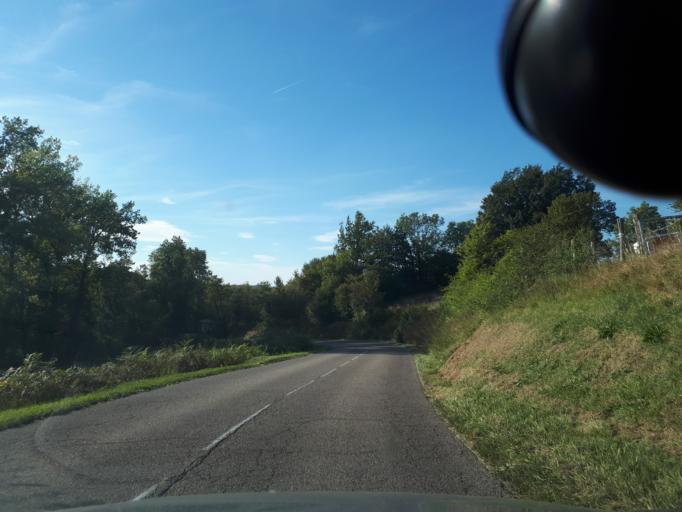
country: FR
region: Rhone-Alpes
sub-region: Departement de l'Isere
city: Maubec
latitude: 45.5383
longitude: 5.2559
